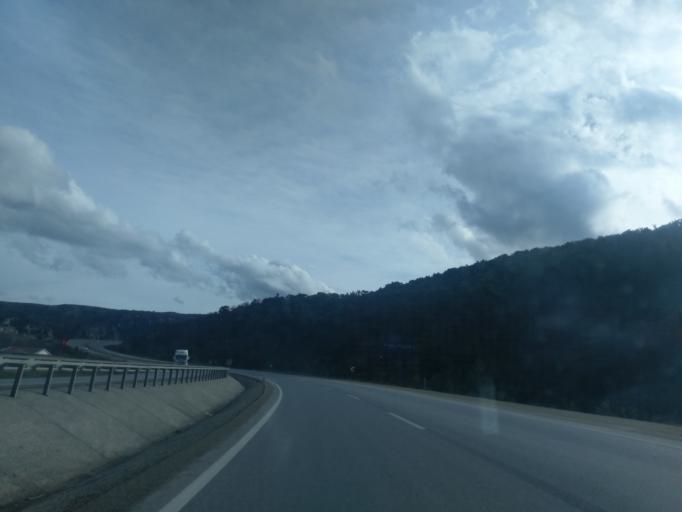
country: TR
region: Kuetahya
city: Sabuncu
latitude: 39.5656
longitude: 30.0718
